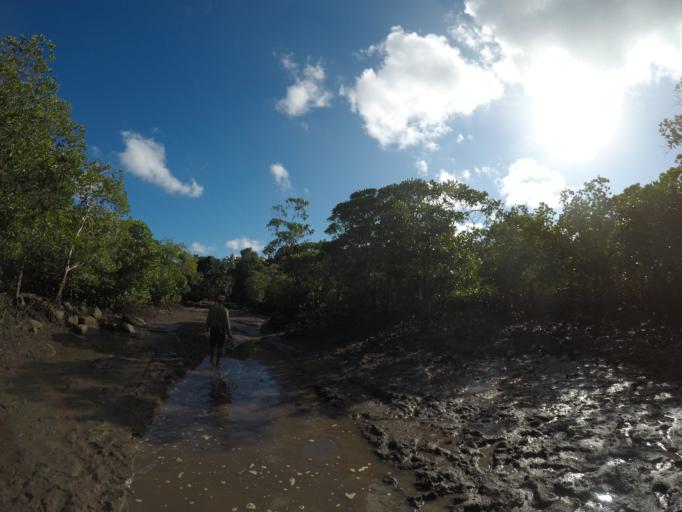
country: TZ
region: Pemba South
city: Mtambile
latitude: -5.3471
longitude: 39.6973
